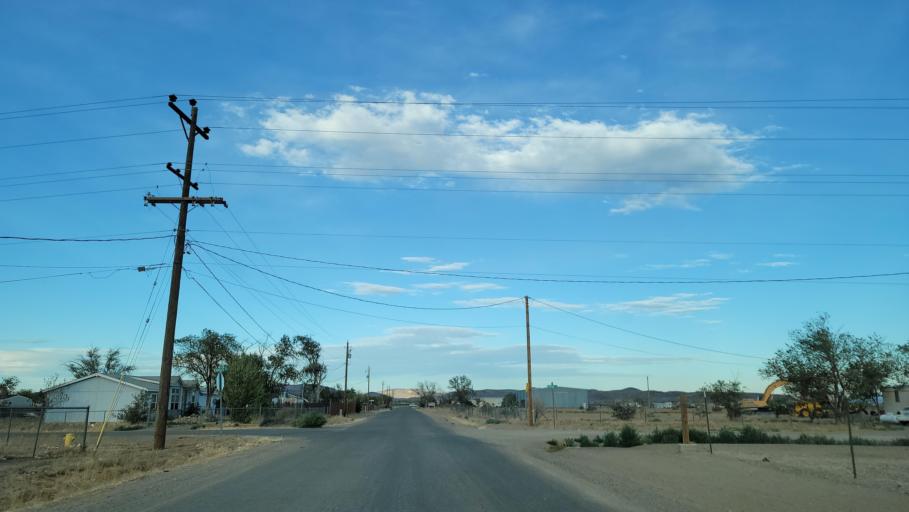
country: US
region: Nevada
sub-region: Lyon County
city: Silver Springs
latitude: 39.4044
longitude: -119.2208
